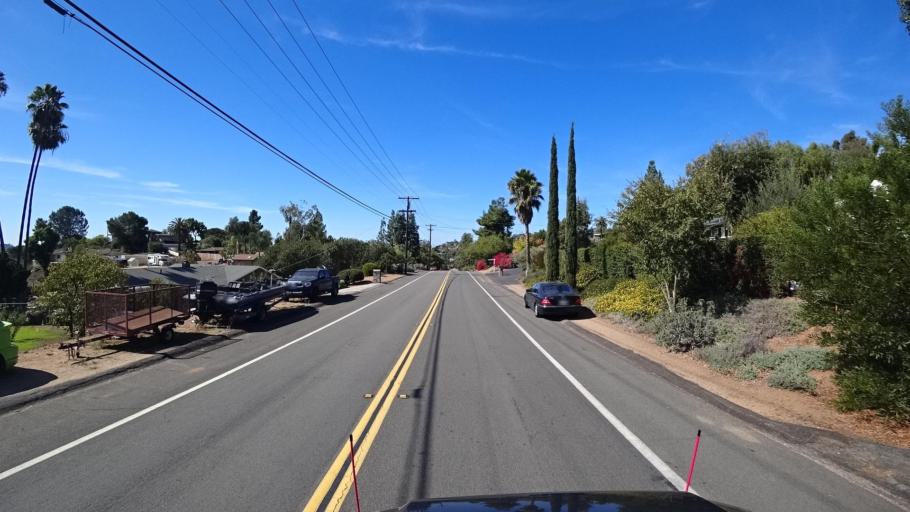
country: US
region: California
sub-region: San Diego County
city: Casa de Oro-Mount Helix
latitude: 32.7578
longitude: -116.9568
